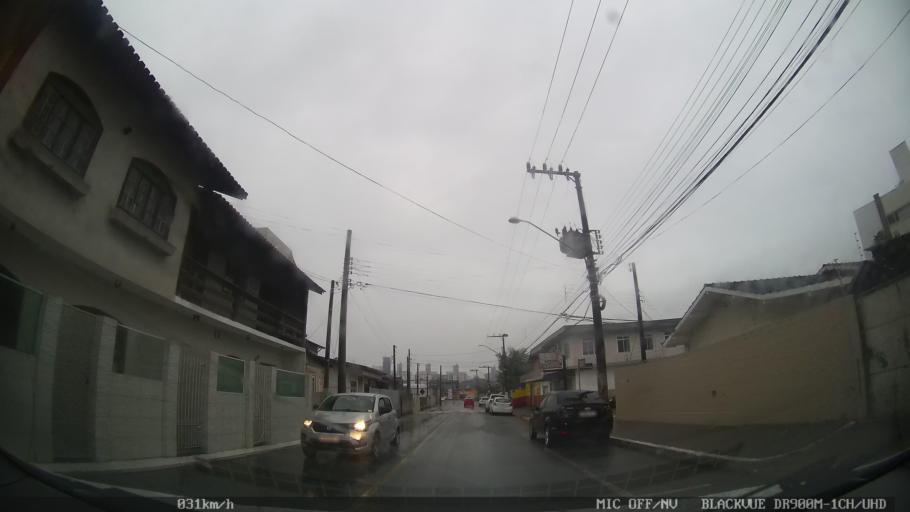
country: BR
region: Santa Catarina
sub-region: Itajai
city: Itajai
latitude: -26.9148
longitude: -48.6826
